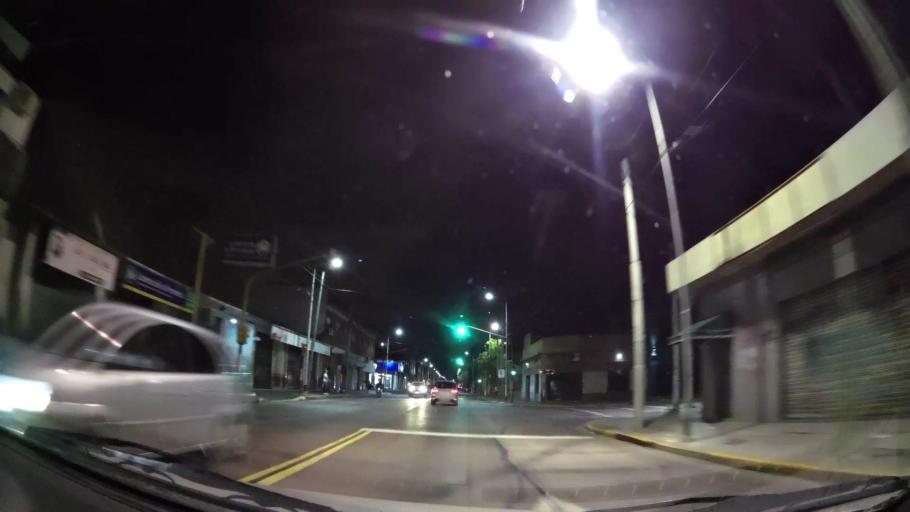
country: AR
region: Buenos Aires
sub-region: Partido de Avellaneda
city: Avellaneda
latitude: -34.6861
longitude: -58.3446
